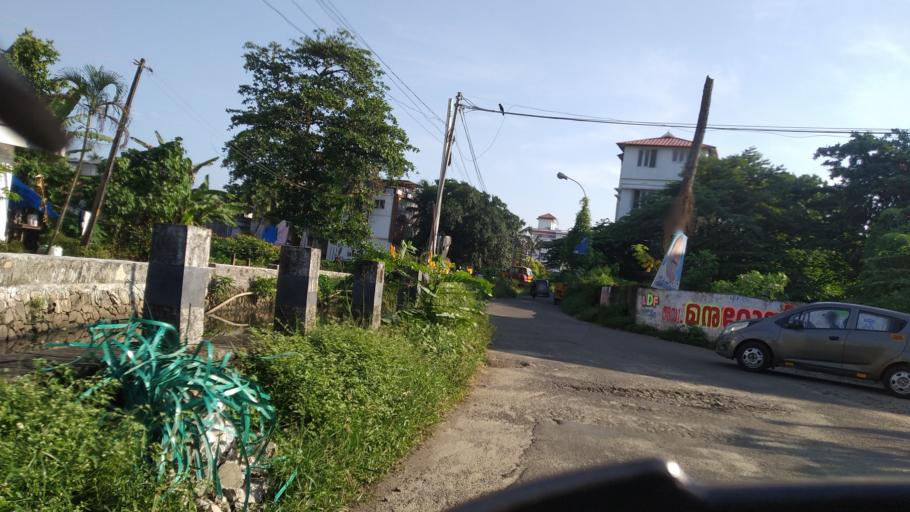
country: IN
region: Kerala
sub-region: Ernakulam
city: Cochin
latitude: 9.9860
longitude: 76.2913
